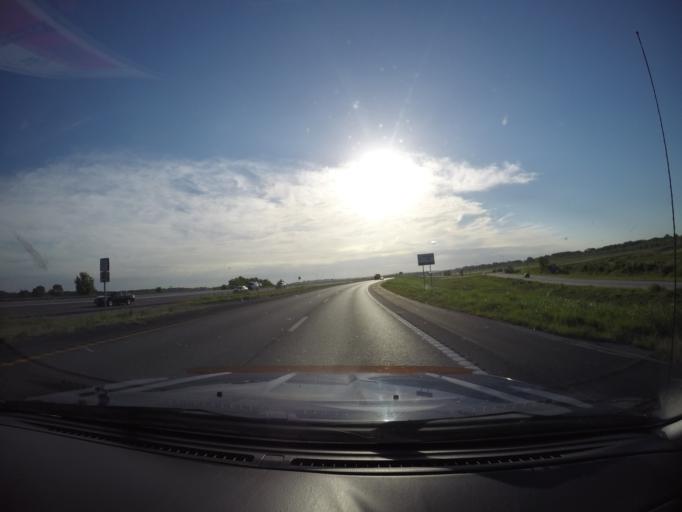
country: US
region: Missouri
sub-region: Platte County
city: Riverside
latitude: 39.1599
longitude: -94.6448
